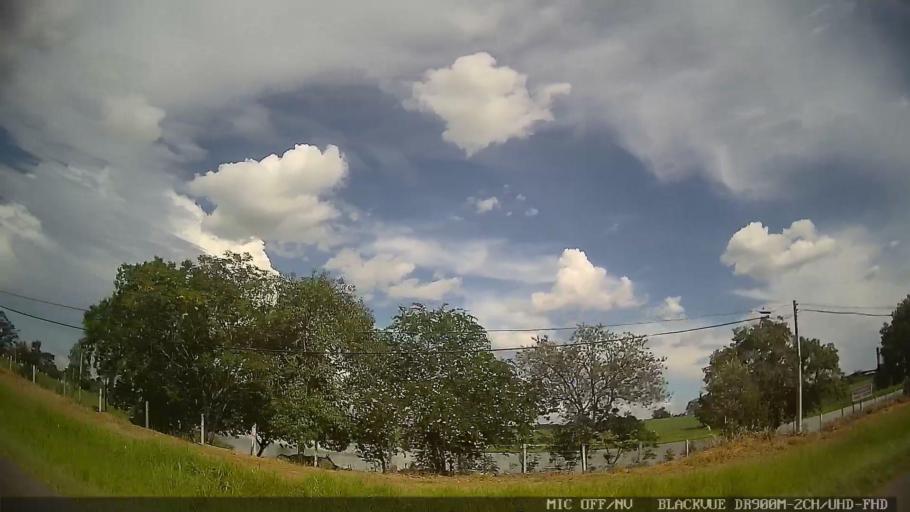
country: BR
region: Sao Paulo
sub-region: Conchas
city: Conchas
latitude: -23.0546
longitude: -47.9601
